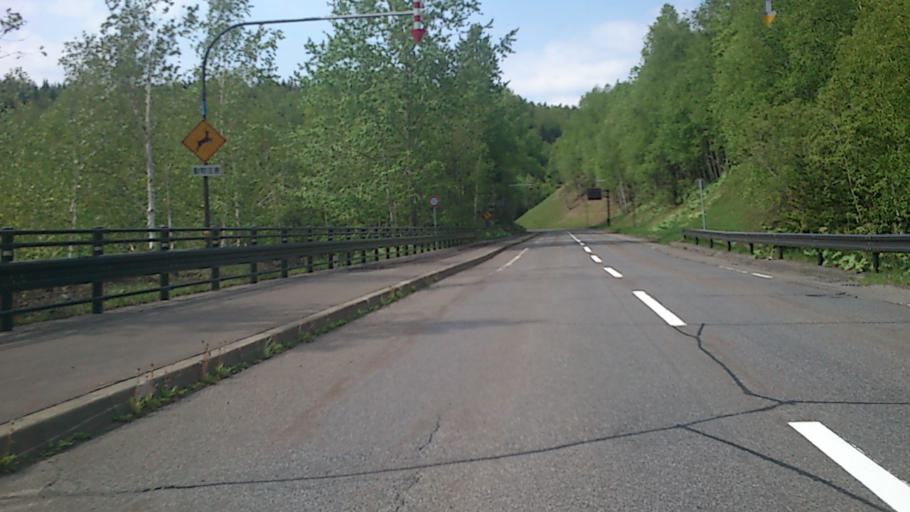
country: JP
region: Hokkaido
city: Kamikawa
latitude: 43.6646
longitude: 143.0358
